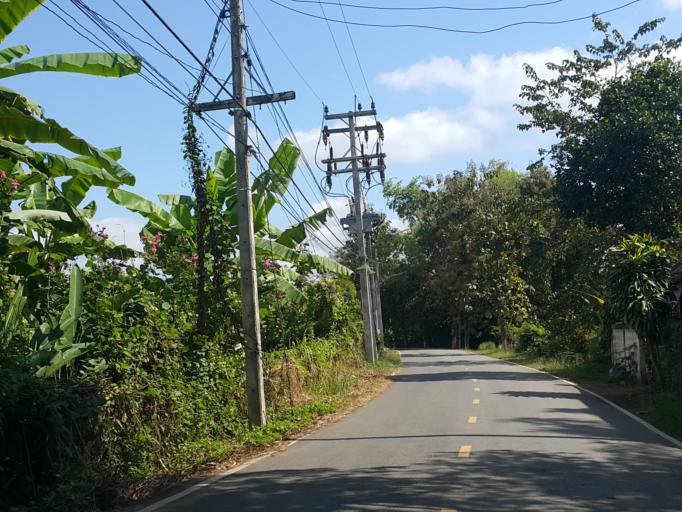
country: TH
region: Lamphun
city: Ban Thi
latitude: 18.5789
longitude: 99.0857
